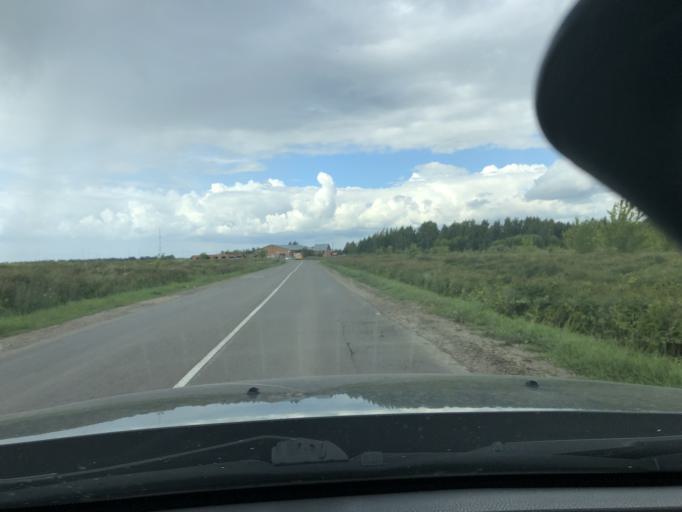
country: RU
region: Tula
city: Kamenetskiy
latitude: 54.0148
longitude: 38.2517
